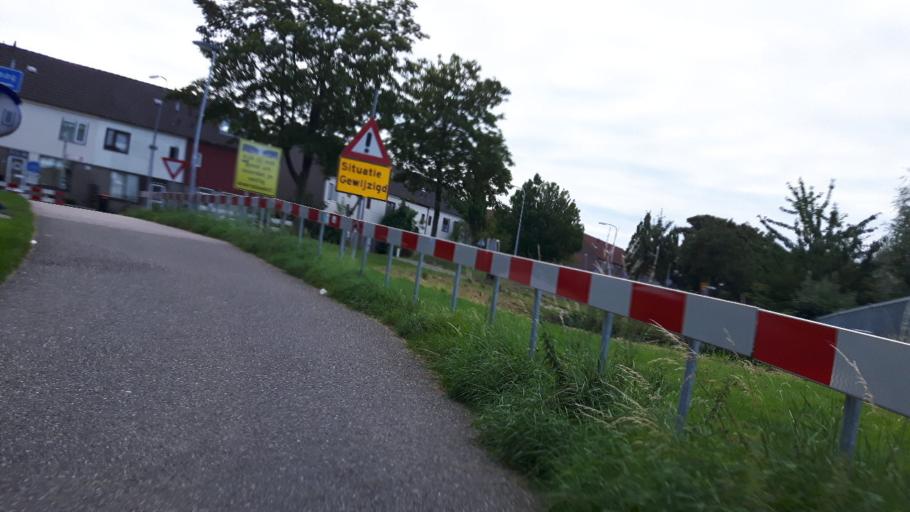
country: NL
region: North Holland
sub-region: Gemeente Hoorn
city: Hoorn
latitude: 52.6684
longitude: 5.0385
